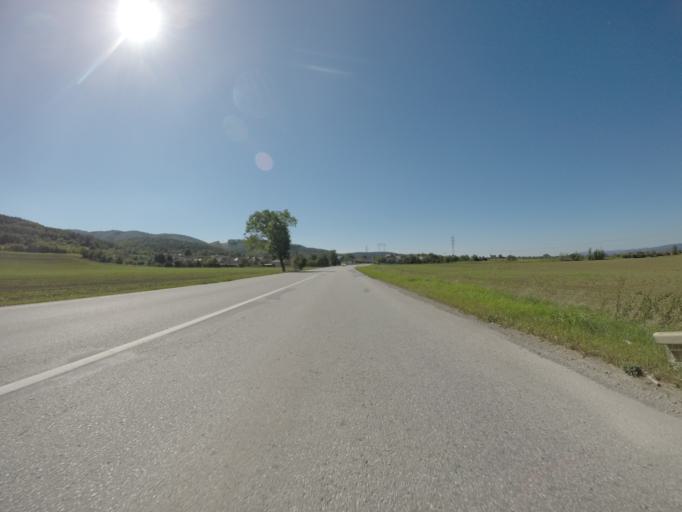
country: SK
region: Nitriansky
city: Ilava
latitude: 49.0194
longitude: 18.2773
